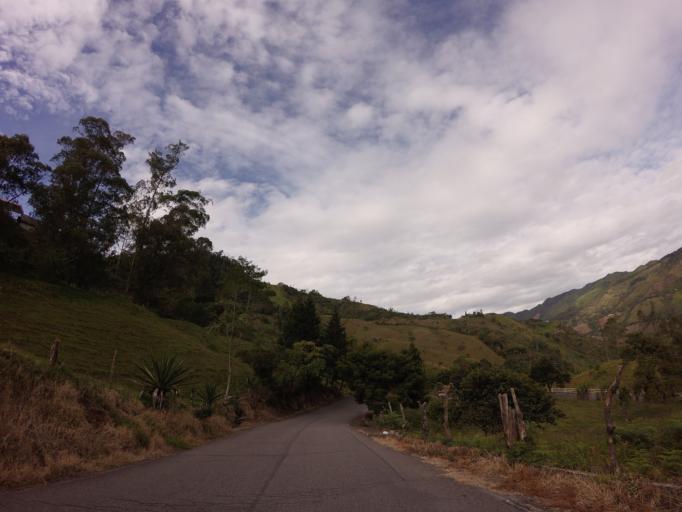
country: CO
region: Tolima
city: Casabianca
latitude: 5.1411
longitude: -75.1288
